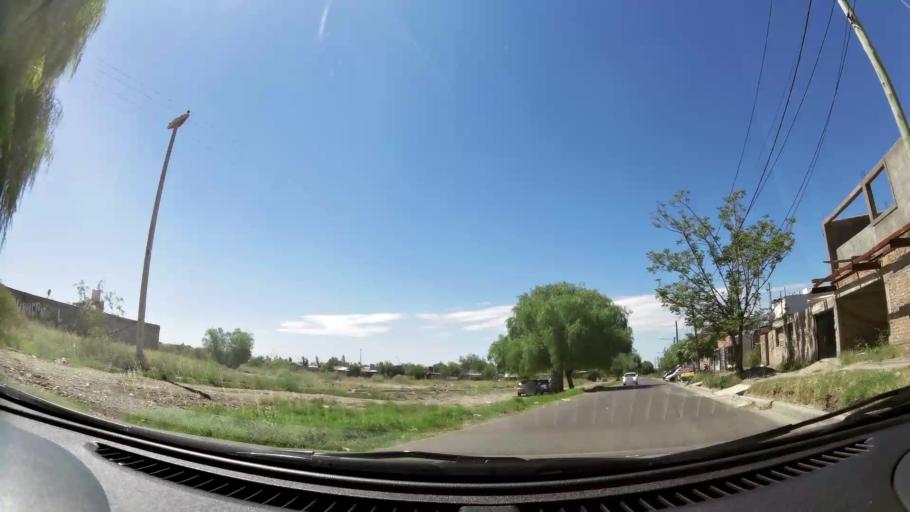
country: AR
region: Mendoza
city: Las Heras
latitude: -32.8410
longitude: -68.8642
